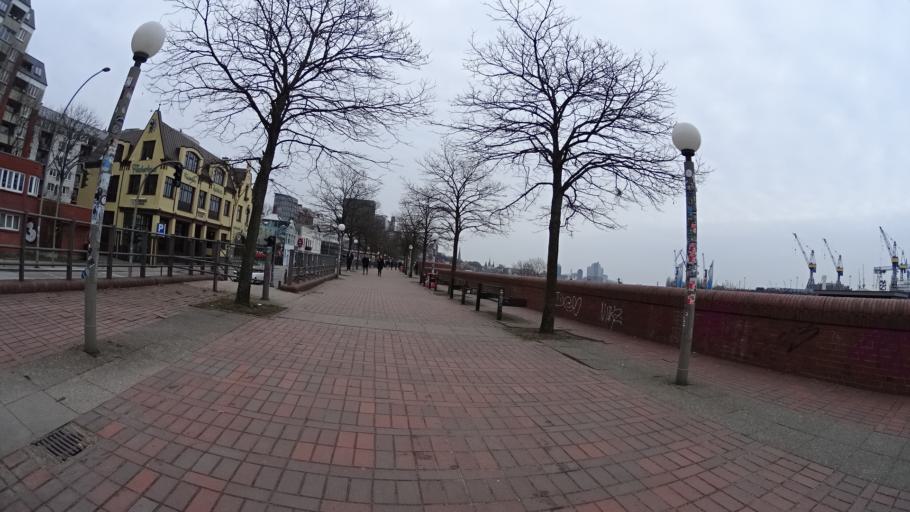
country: DE
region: Hamburg
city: St. Pauli
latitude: 53.5455
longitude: 9.9548
